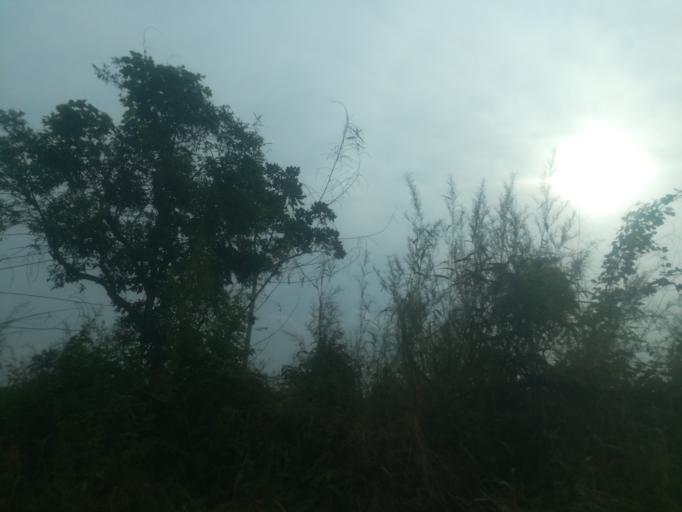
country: NG
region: Ogun
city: Ayetoro
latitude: 7.2395
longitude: 3.1272
